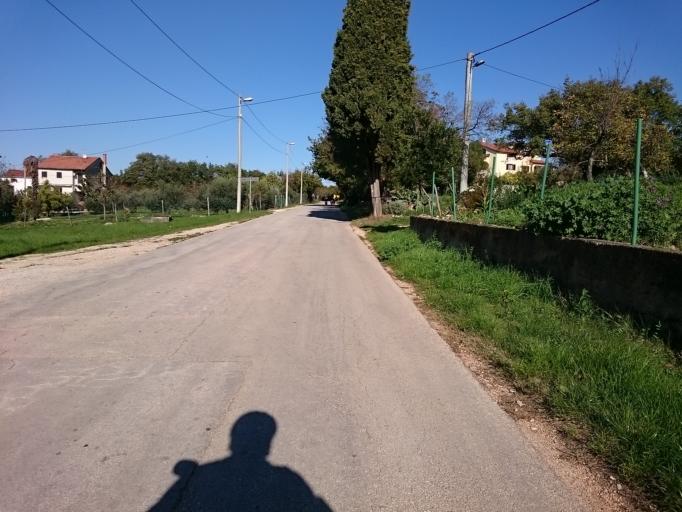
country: HR
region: Istarska
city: Umag
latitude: 45.4520
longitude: 13.5373
